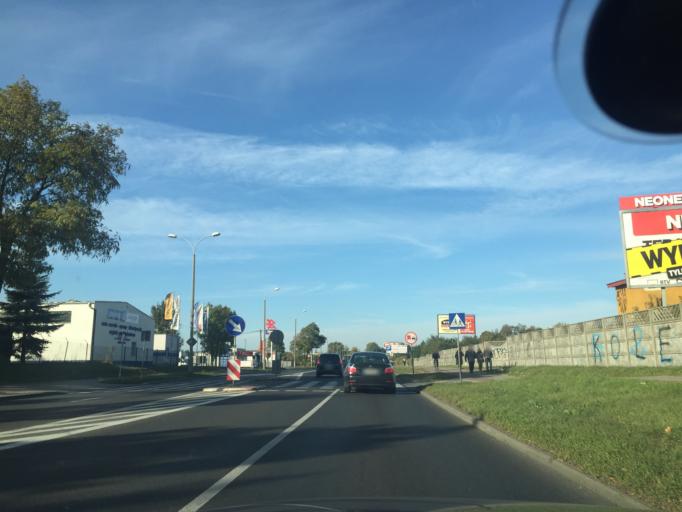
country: PL
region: Kujawsko-Pomorskie
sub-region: Powiat inowroclawski
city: Inowroclaw
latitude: 52.7826
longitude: 18.2604
